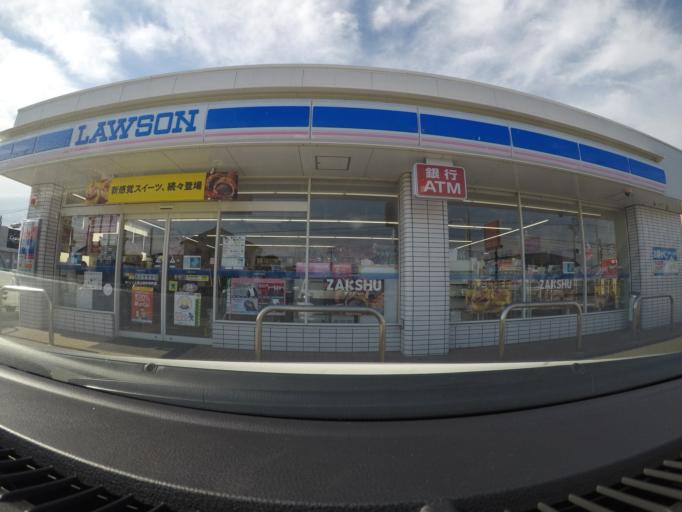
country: JP
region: Kochi
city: Kochi-shi
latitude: 33.6023
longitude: 133.6765
